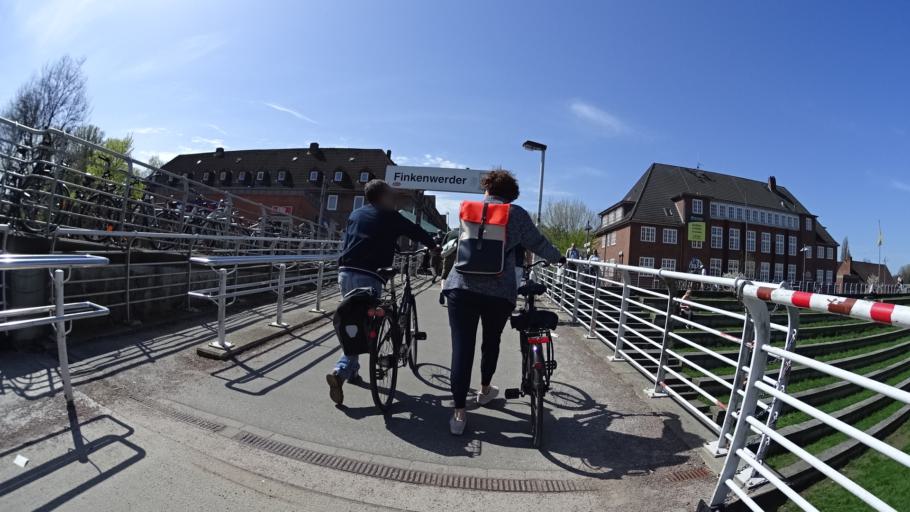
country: DE
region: Hamburg
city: Altona
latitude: 53.5361
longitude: 9.8784
